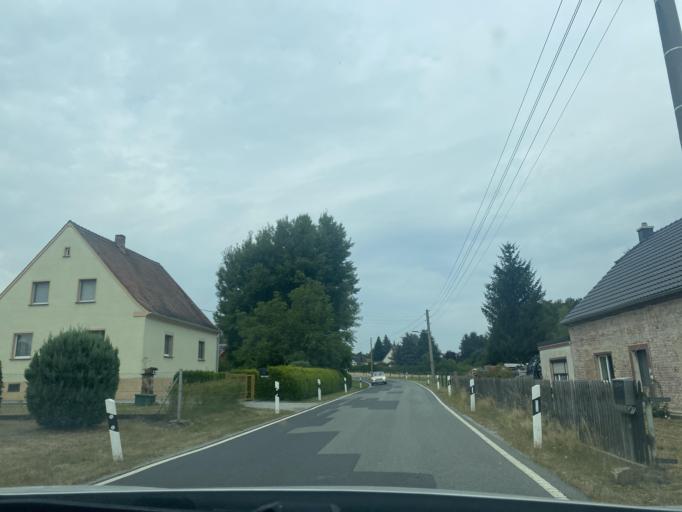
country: DE
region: Saxony
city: Radibor
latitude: 51.3031
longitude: 14.4059
